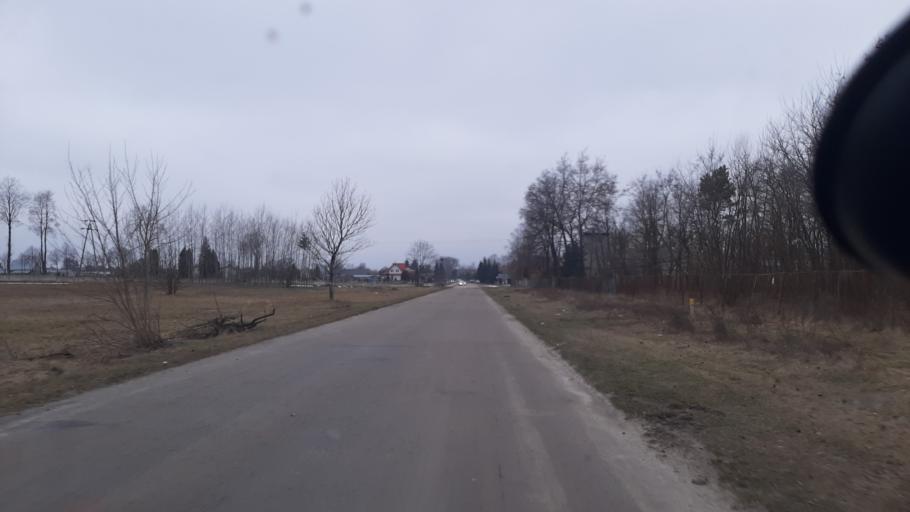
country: PL
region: Lublin Voivodeship
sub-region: Powiat wlodawski
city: Wlodawa
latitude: 51.5211
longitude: 23.5828
